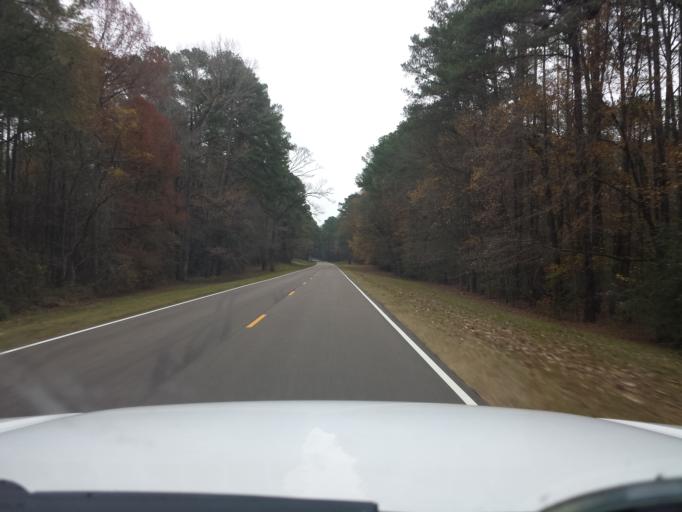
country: US
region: Mississippi
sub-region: Madison County
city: Canton
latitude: 32.5459
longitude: -89.9431
